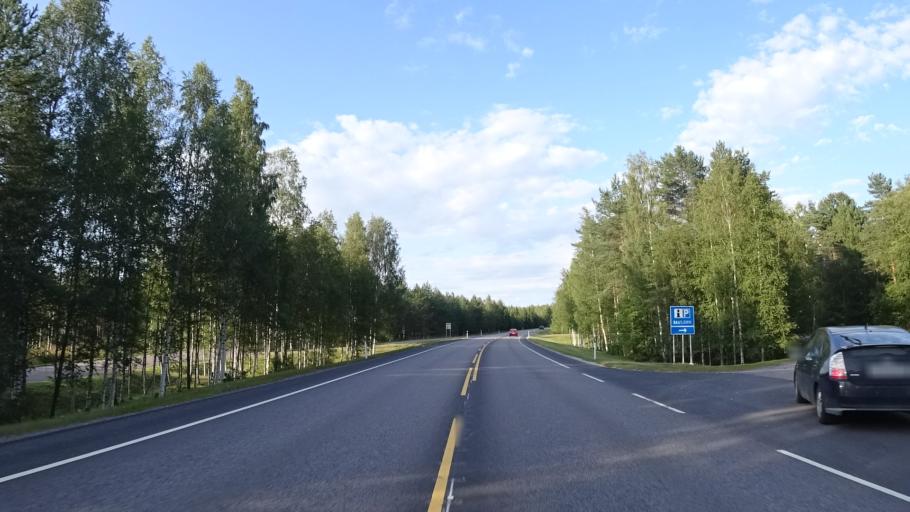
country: FI
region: South Karelia
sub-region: Imatra
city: Rautjaervi
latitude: 61.3251
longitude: 29.1076
